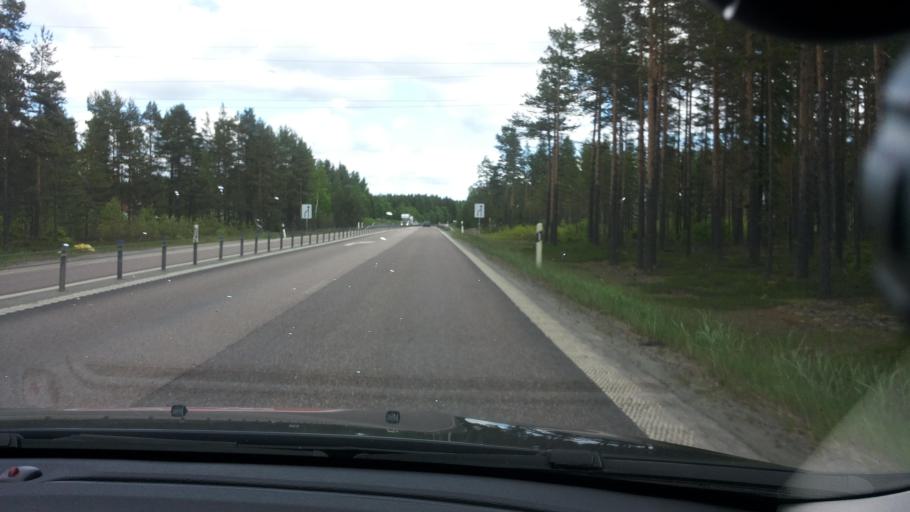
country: SE
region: Vaesternorrland
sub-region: Timra Kommun
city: Bergeforsen
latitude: 62.5071
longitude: 17.3581
